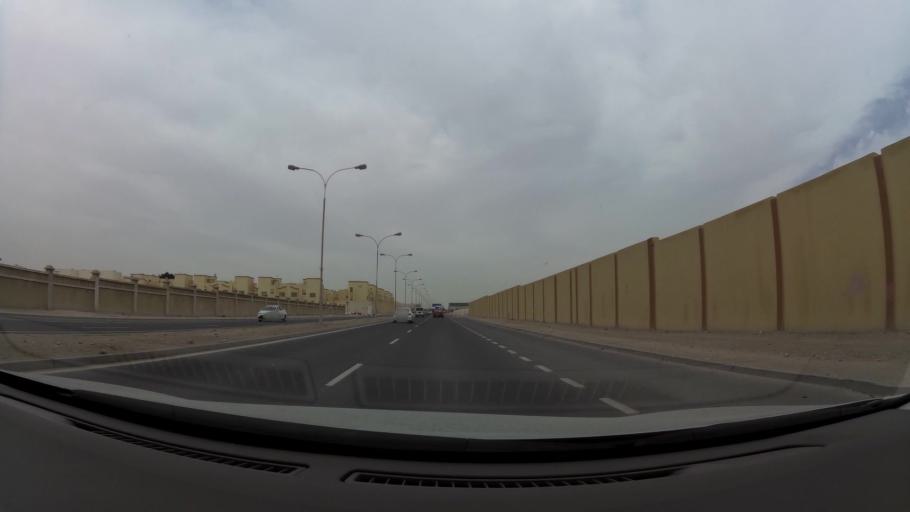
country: QA
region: Baladiyat ar Rayyan
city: Ar Rayyan
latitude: 25.2279
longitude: 51.4488
